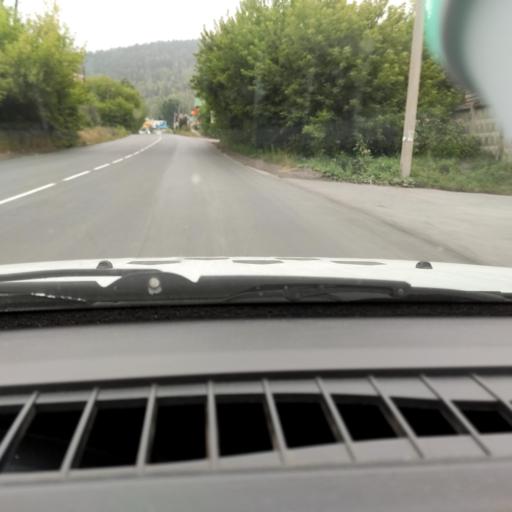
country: RU
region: Chelyabinsk
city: Miass
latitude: 55.0313
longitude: 60.1211
